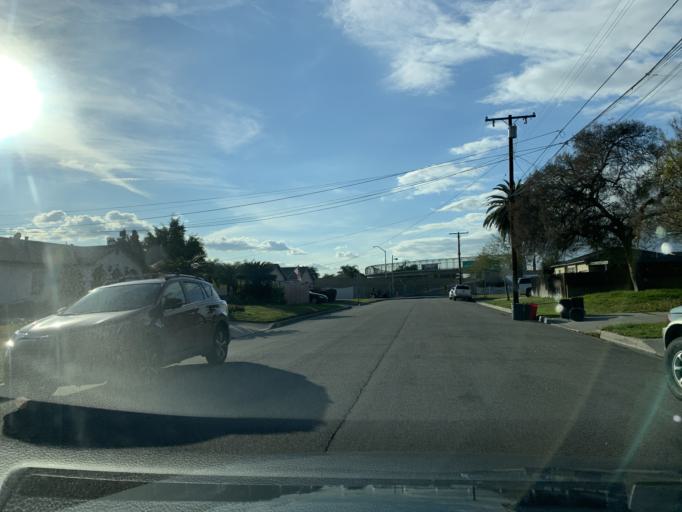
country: US
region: California
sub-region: Los Angeles County
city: Azusa
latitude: 34.1244
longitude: -117.9127
